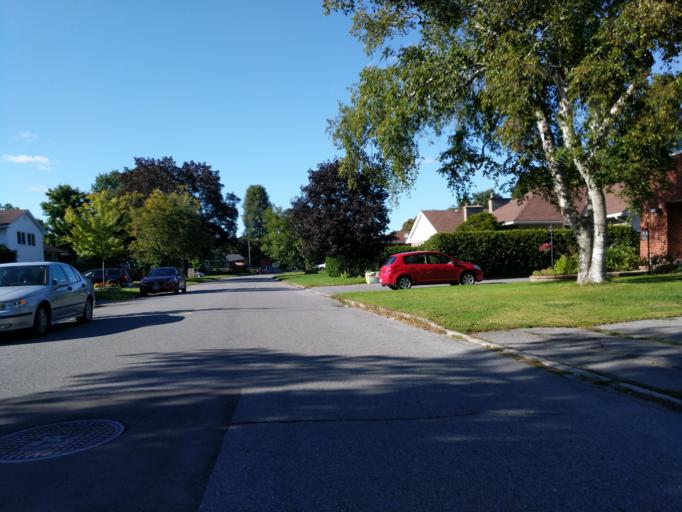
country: CA
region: Ontario
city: Ottawa
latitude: 45.3620
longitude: -75.7460
